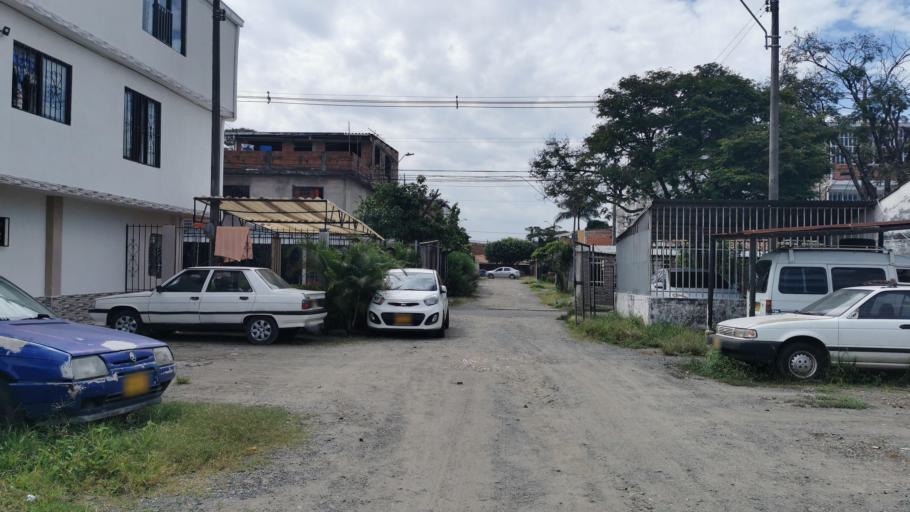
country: CO
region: Valle del Cauca
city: Jamundi
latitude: 3.2655
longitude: -76.5363
